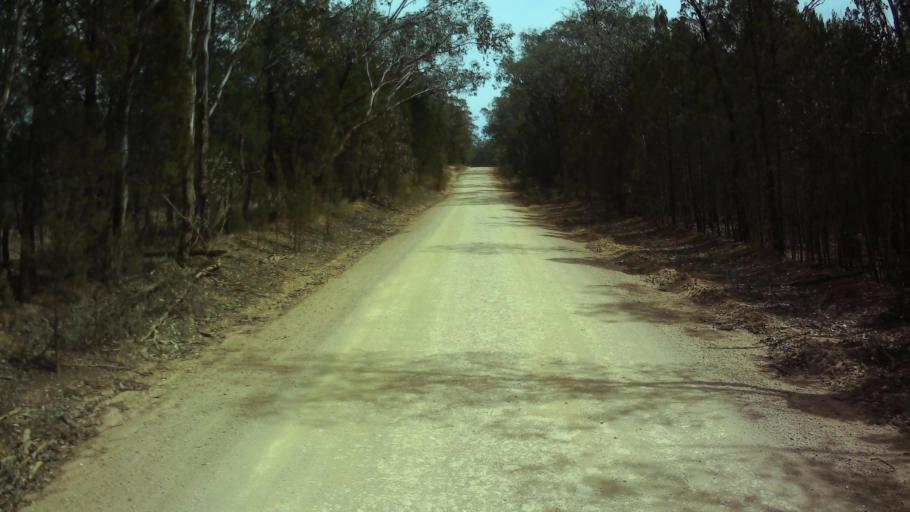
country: AU
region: New South Wales
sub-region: Weddin
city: Grenfell
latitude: -33.9080
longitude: 148.4100
